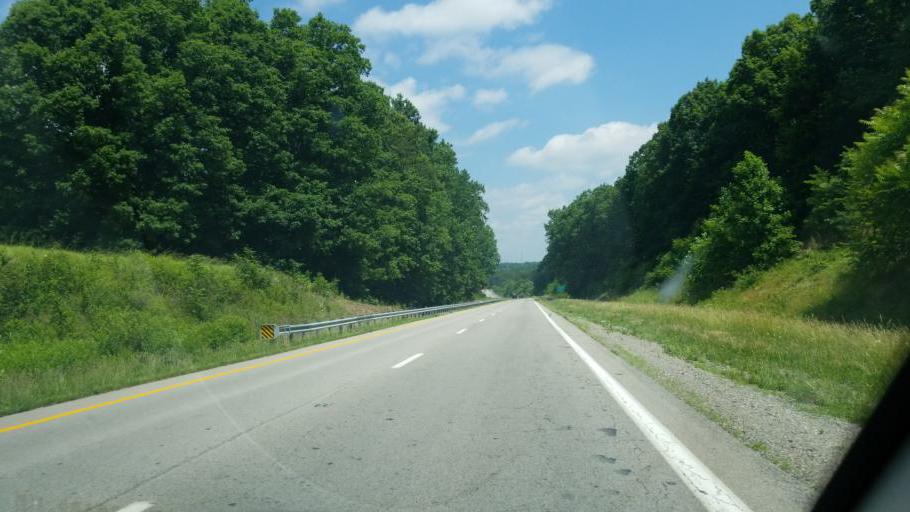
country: US
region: Virginia
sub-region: Pittsylvania County
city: Motley
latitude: 37.0888
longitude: -79.3319
